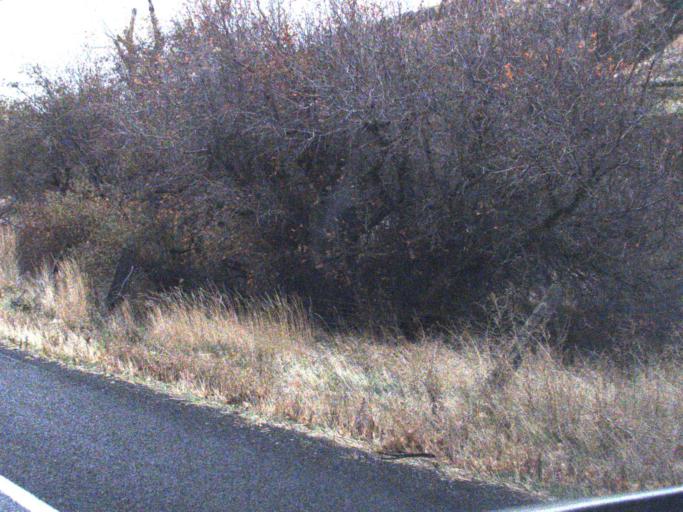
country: US
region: Washington
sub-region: Walla Walla County
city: Waitsburg
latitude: 46.2893
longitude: -118.0894
